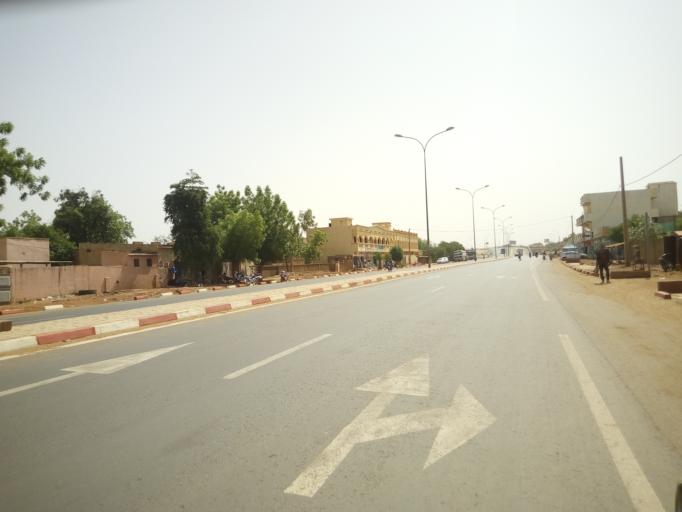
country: ML
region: Segou
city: Segou
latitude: 13.4361
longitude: -6.2427
